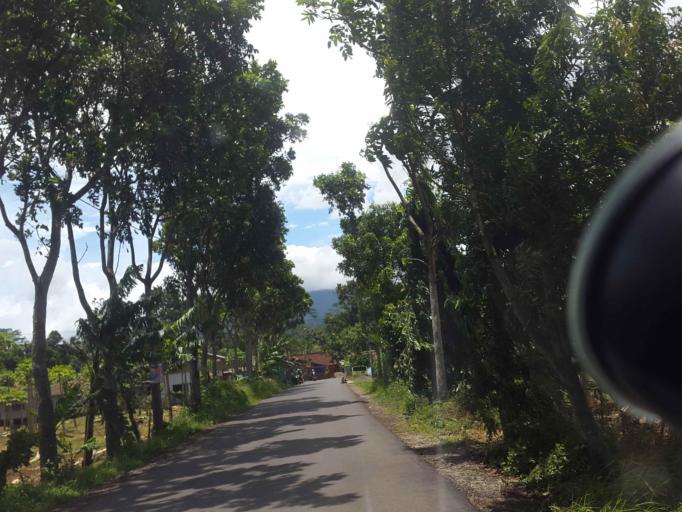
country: ID
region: Central Java
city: Sangkalputung
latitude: -7.4044
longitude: 109.0955
